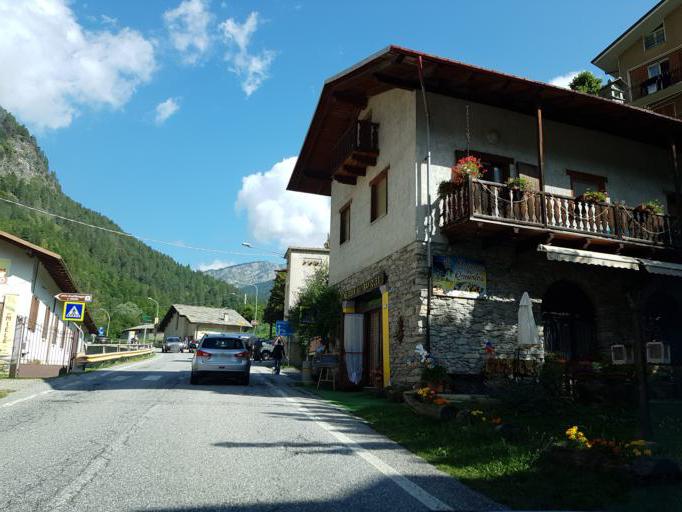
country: IT
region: Piedmont
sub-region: Provincia di Cuneo
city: Casteldelfino
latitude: 44.5902
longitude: 7.0688
